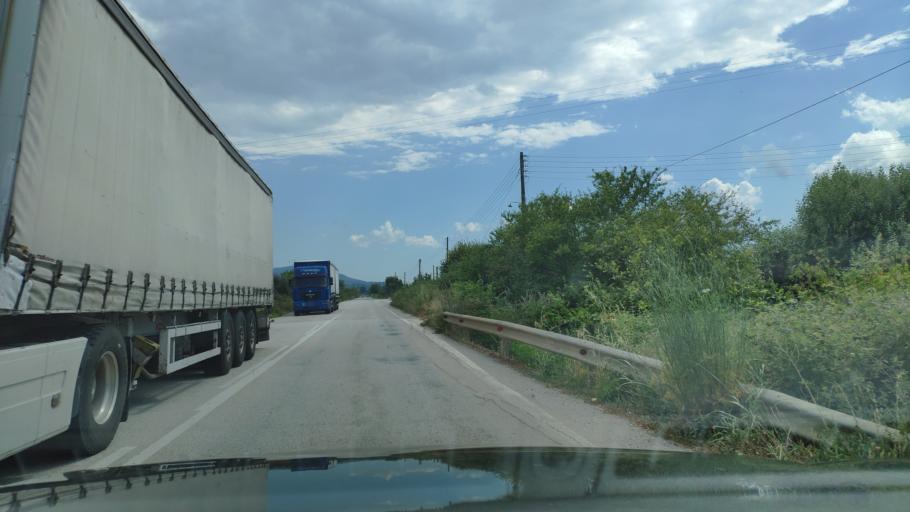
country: GR
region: West Greece
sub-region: Nomos Aitolias kai Akarnanias
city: Krikellos
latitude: 38.9393
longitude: 21.1769
